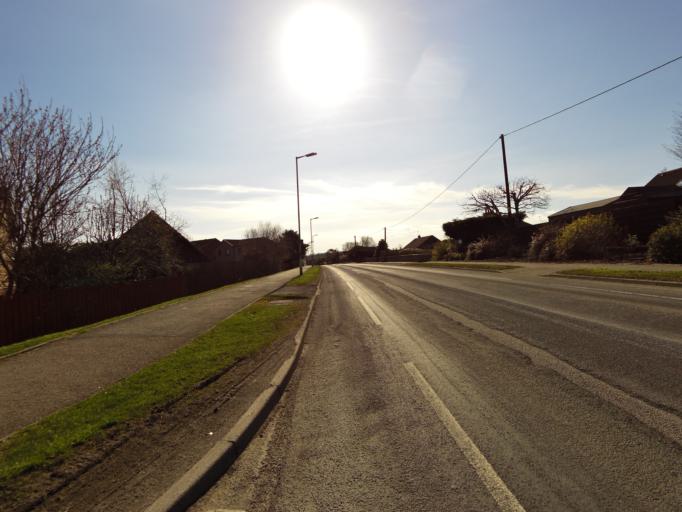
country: GB
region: Scotland
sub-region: Aberdeenshire
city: Portlethen
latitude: 57.0564
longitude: -2.1417
